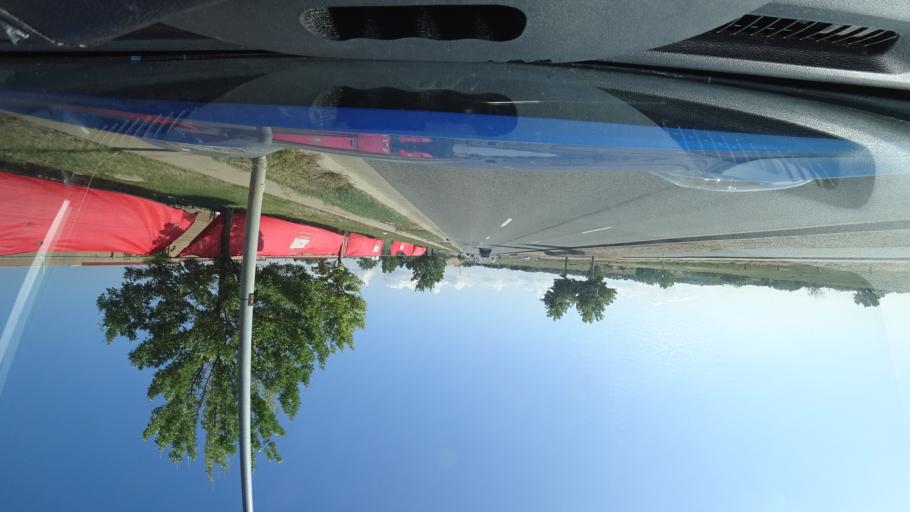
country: US
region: Colorado
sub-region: Adams County
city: Aurora
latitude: 39.7132
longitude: -104.7913
